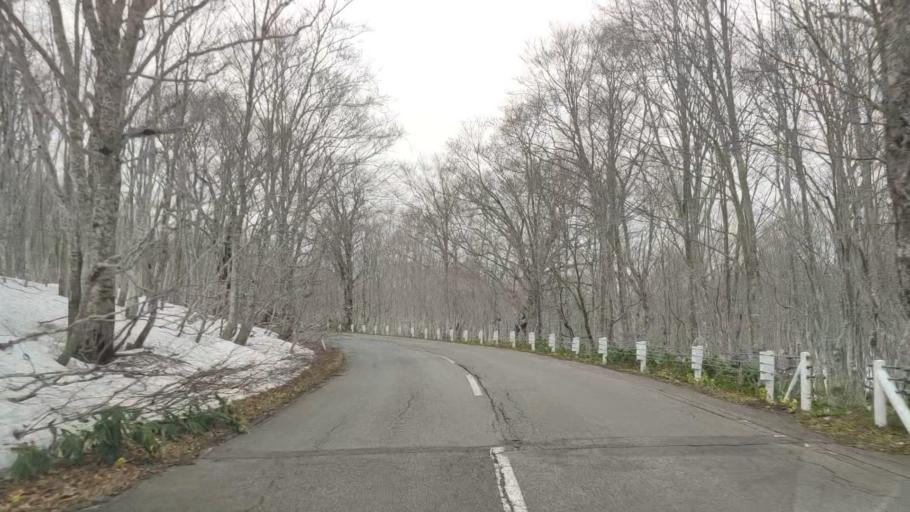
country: JP
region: Aomori
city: Aomori Shi
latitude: 40.6492
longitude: 140.9451
